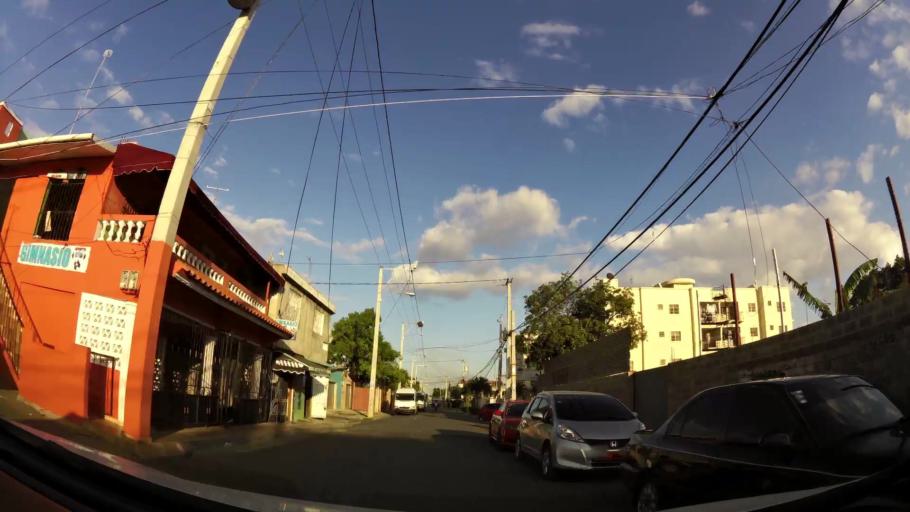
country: DO
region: Santo Domingo
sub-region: Santo Domingo
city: Santo Domingo Este
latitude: 18.4828
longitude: -69.8375
